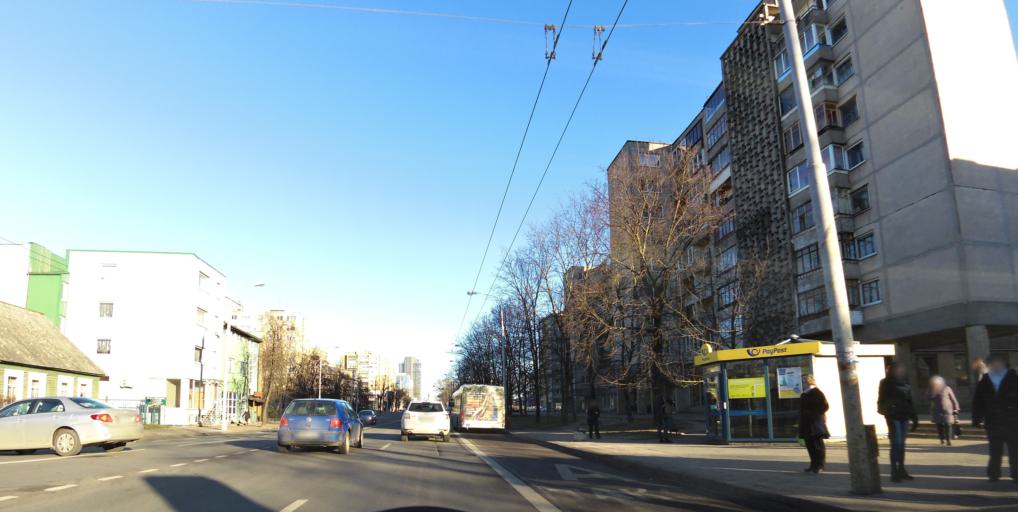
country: LT
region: Vilnius County
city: Vilkpede
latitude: 54.6739
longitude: 25.2483
